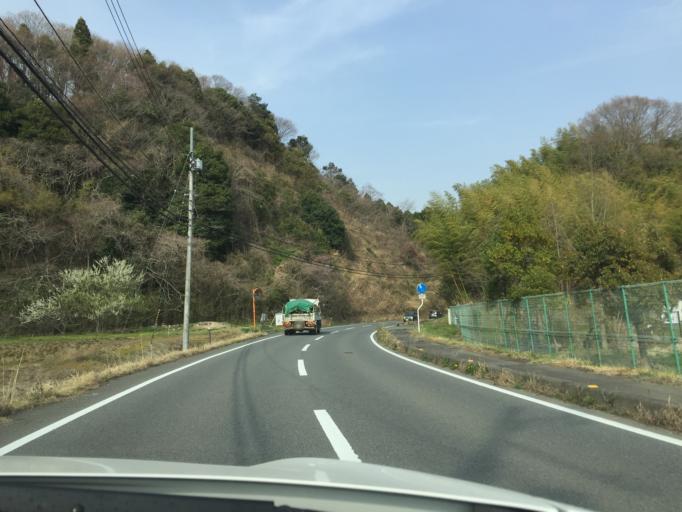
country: JP
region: Fukushima
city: Iwaki
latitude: 36.9590
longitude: 140.8284
